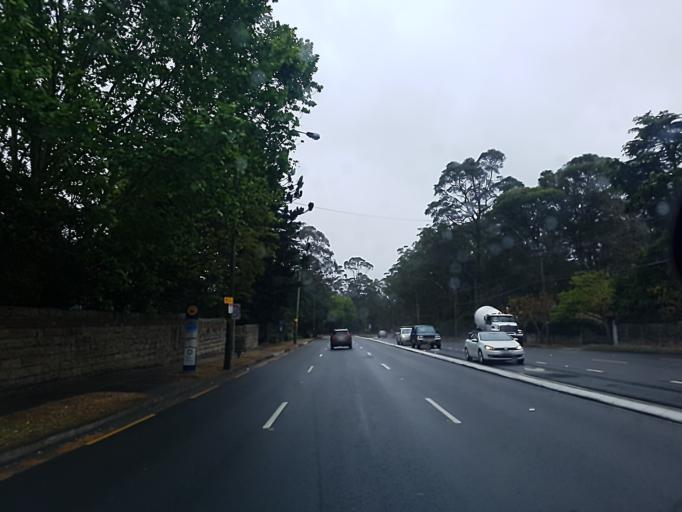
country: AU
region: New South Wales
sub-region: City of Sydney
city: Pymble
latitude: -33.7382
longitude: 151.1525
